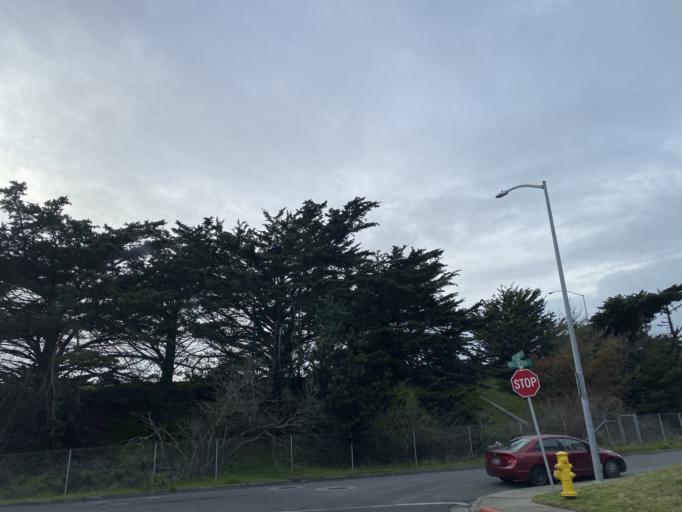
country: US
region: California
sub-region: San Mateo County
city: Broadmoor
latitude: 37.6539
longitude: -122.4894
